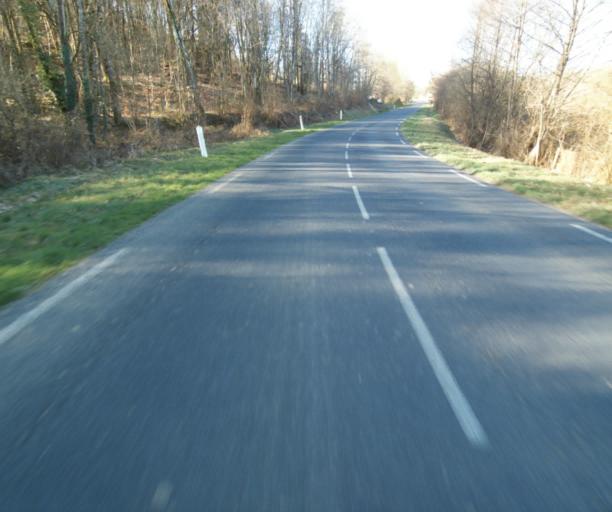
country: FR
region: Limousin
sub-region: Departement de la Correze
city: Seilhac
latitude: 45.4012
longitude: 1.7201
